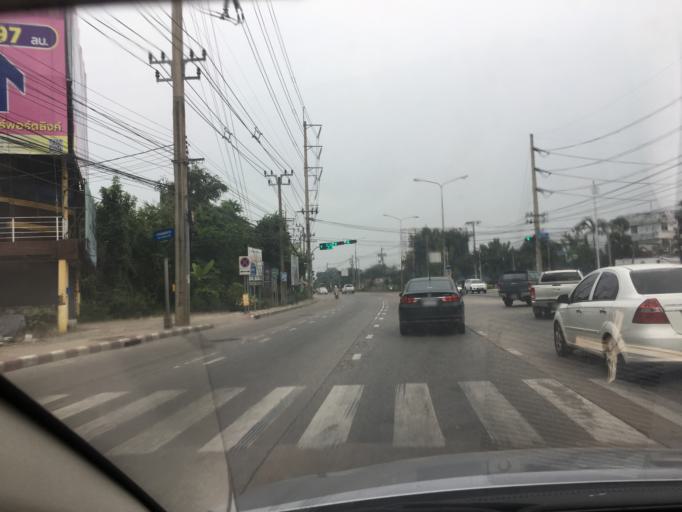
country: TH
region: Bangkok
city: Lat Krabang
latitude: 13.7507
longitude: 100.7945
